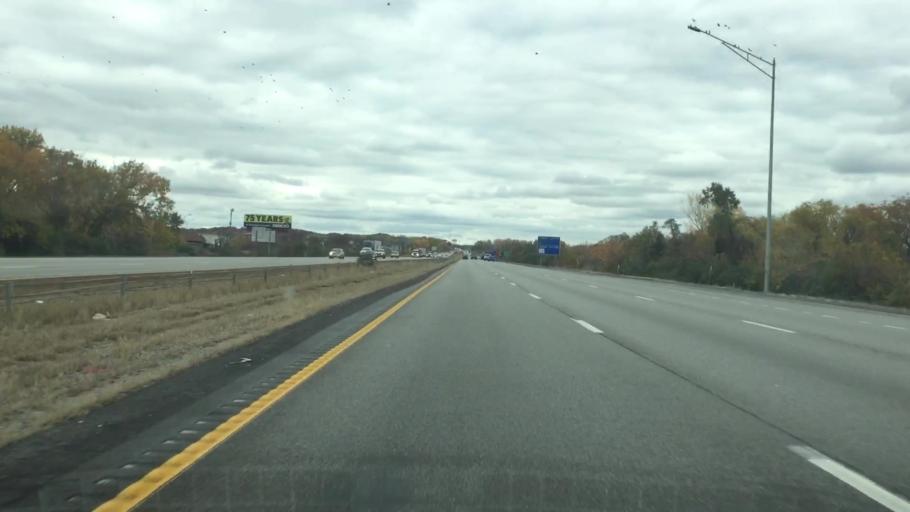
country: US
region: Missouri
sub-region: Jackson County
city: Sugar Creek
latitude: 39.1347
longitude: -94.4989
